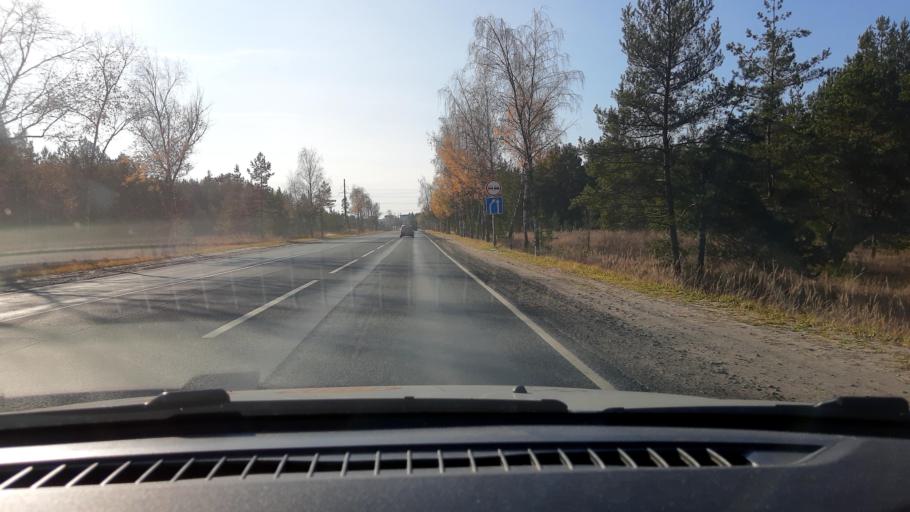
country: RU
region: Nizjnij Novgorod
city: Dzerzhinsk
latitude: 56.2698
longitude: 43.4723
